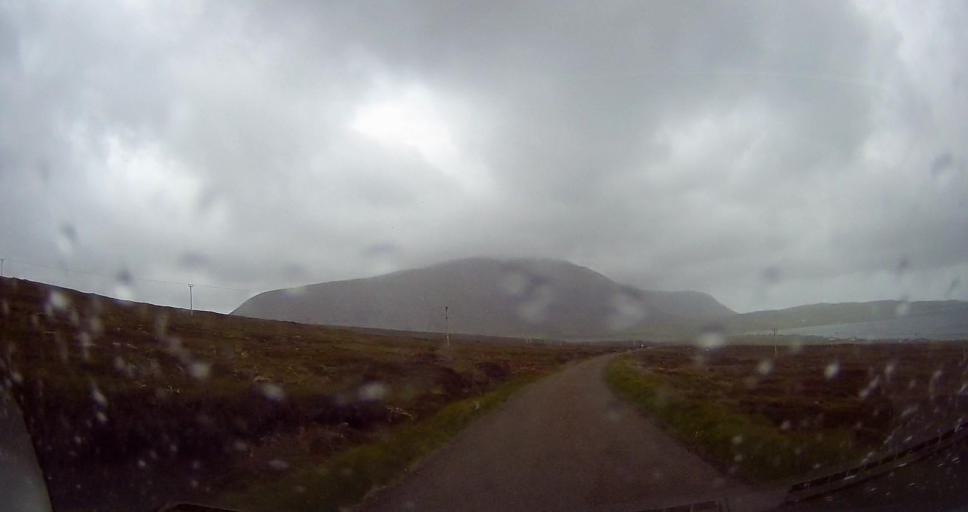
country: GB
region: Scotland
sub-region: Orkney Islands
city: Stromness
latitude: 58.9000
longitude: -3.2810
